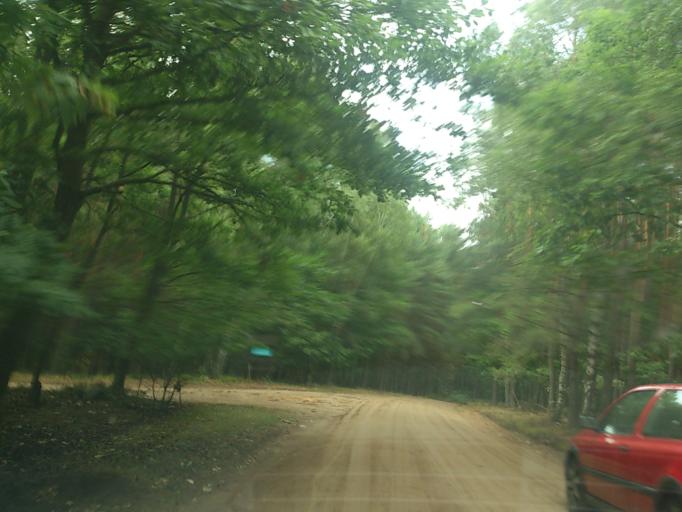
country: PL
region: Greater Poland Voivodeship
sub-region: Powiat poznanski
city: Kobylnica
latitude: 52.5292
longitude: 17.1168
